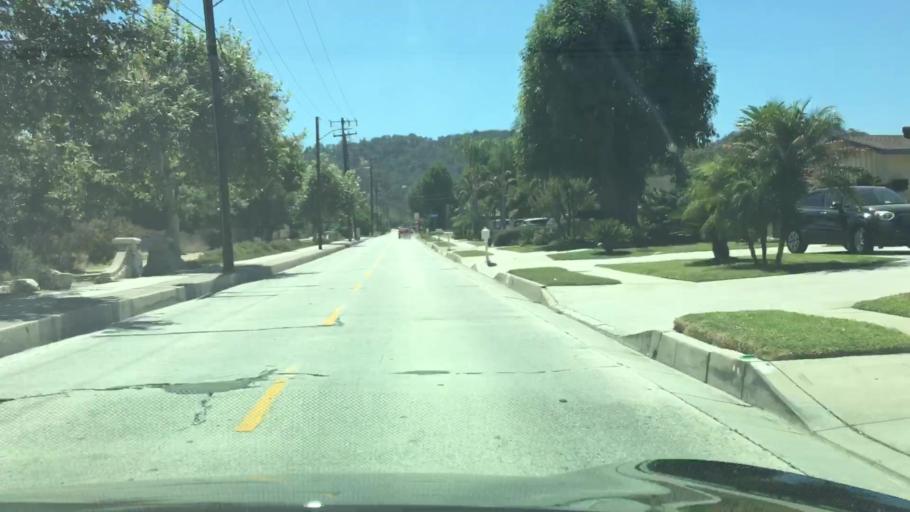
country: US
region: California
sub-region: Los Angeles County
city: Avocado Heights
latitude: 34.0143
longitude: -117.9912
